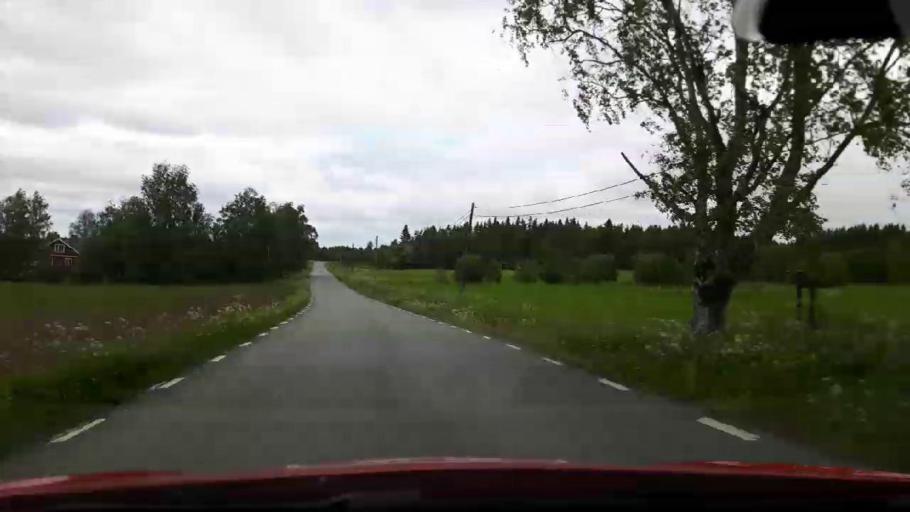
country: SE
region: Jaemtland
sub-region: Krokoms Kommun
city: Krokom
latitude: 63.2590
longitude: 14.5381
